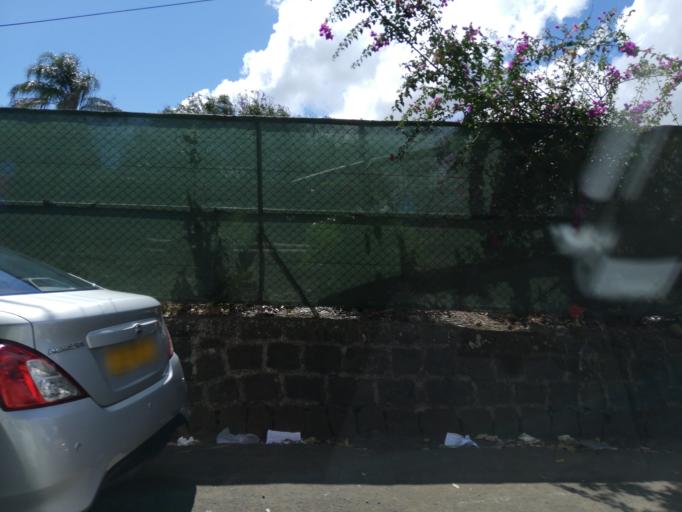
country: MU
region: Moka
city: Moka
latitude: -20.2265
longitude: 57.4672
